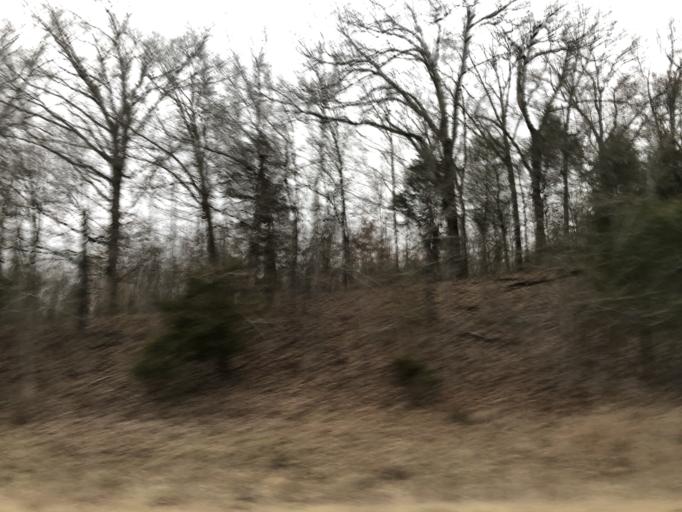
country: US
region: Illinois
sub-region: Johnson County
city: Vienna
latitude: 37.3472
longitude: -88.7871
